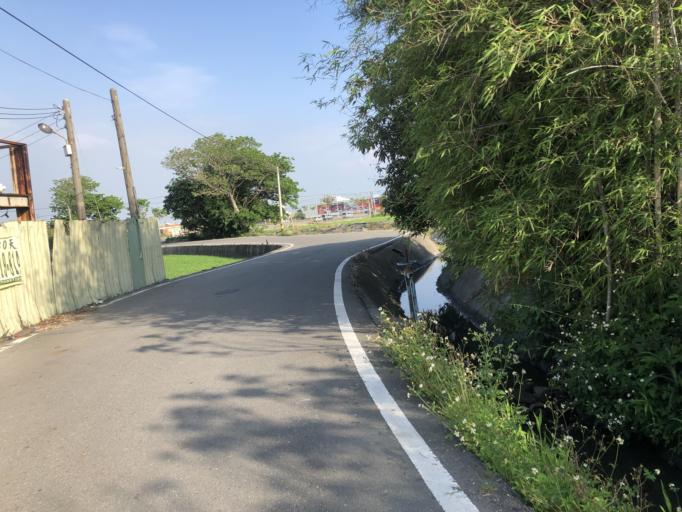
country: TW
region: Taiwan
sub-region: Changhua
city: Chang-hua
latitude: 24.0504
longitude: 120.4679
